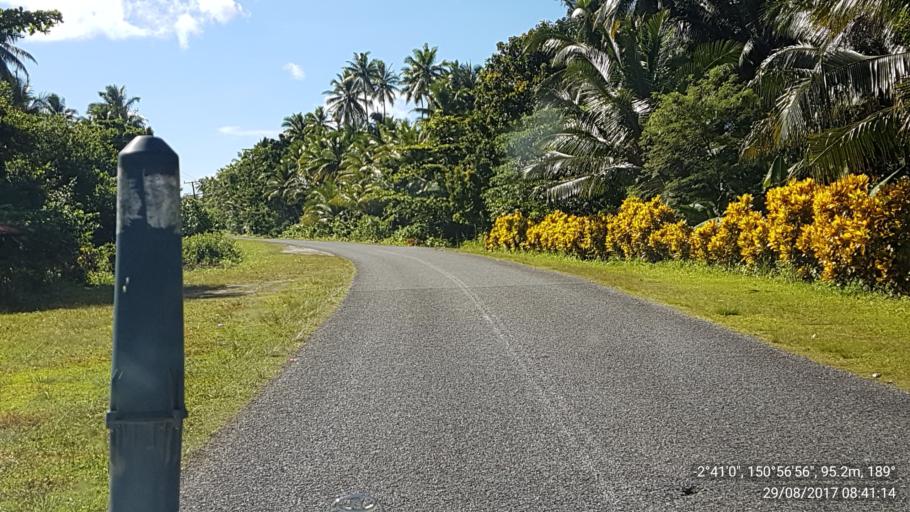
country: PG
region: New Ireland
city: Kavieng
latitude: -2.6833
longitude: 150.9492
